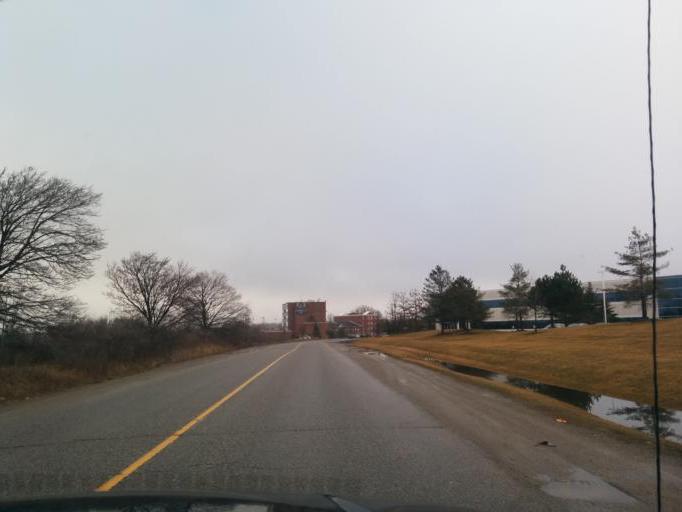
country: CA
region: Ontario
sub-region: Halton
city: Milton
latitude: 43.5255
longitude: -79.9111
